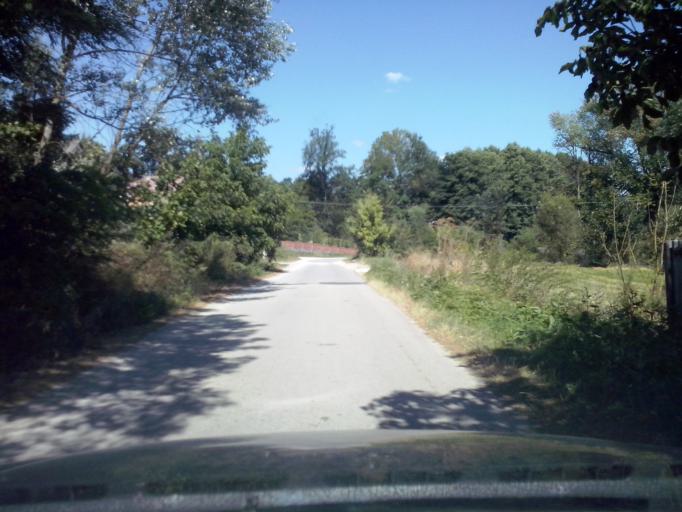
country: PL
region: Swietokrzyskie
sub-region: Powiat buski
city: Gnojno
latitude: 50.6072
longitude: 20.8895
